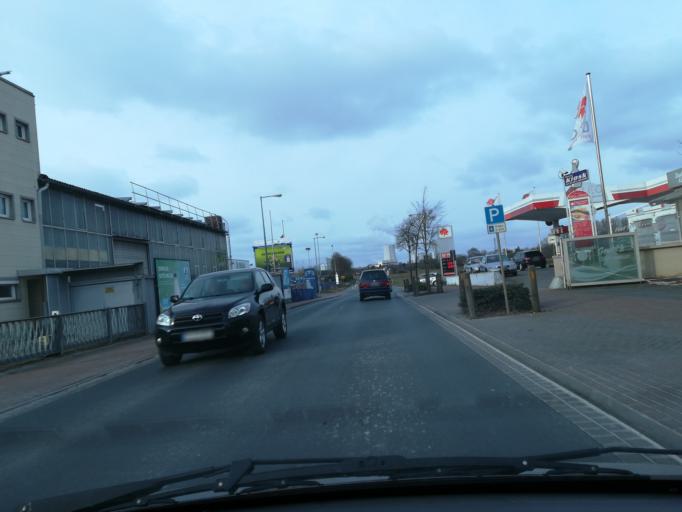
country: DE
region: Lower Saxony
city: Auf der Horst
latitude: 52.4050
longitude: 9.6462
